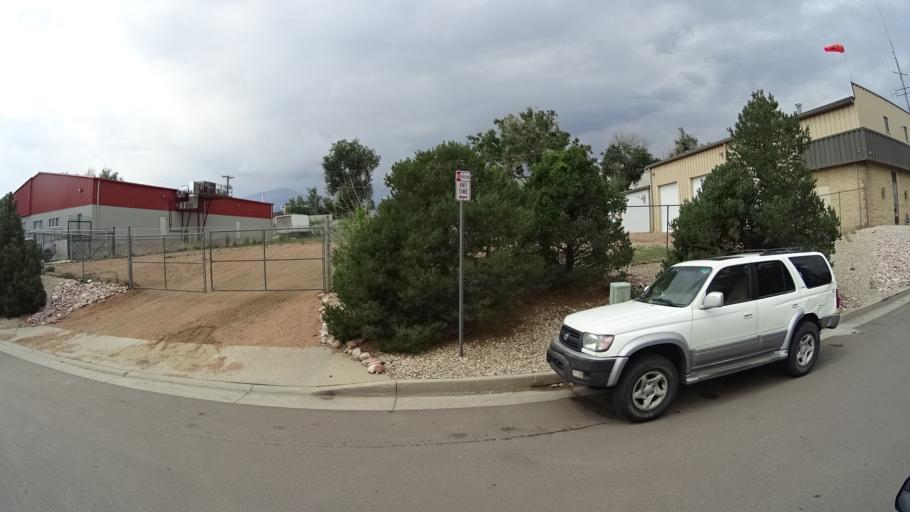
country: US
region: Colorado
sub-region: El Paso County
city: Colorado Springs
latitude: 38.8880
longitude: -104.8307
